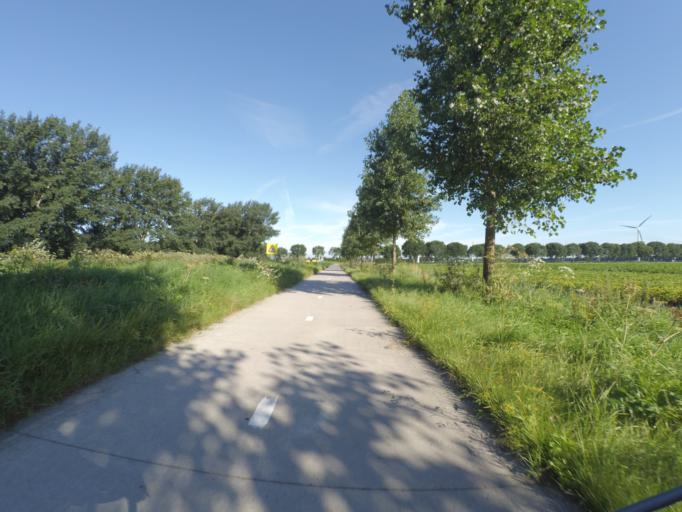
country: NL
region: Flevoland
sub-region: Gemeente Zeewolde
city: Zeewolde
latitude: 52.3613
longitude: 5.4831
